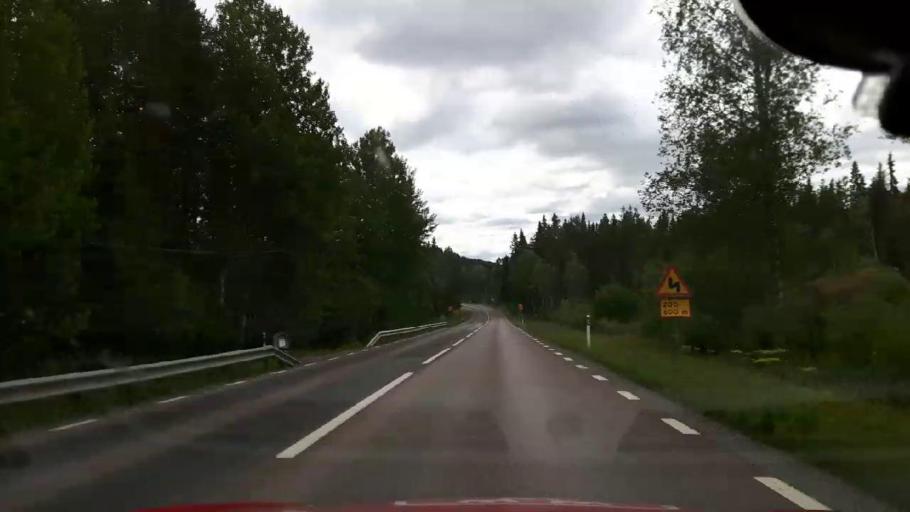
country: SE
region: Jaemtland
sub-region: OEstersunds Kommun
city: Brunflo
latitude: 63.0196
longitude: 14.9322
